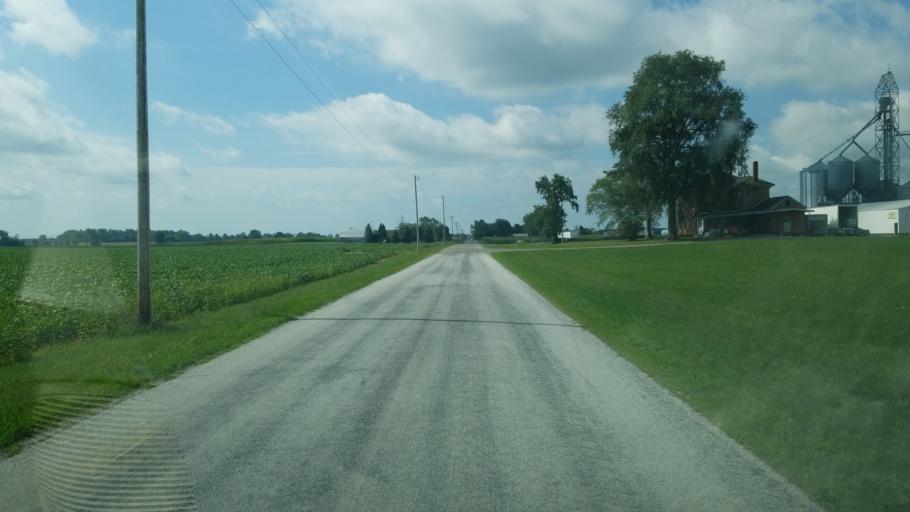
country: US
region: Ohio
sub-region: Hardin County
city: Kenton
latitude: 40.6002
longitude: -83.4446
